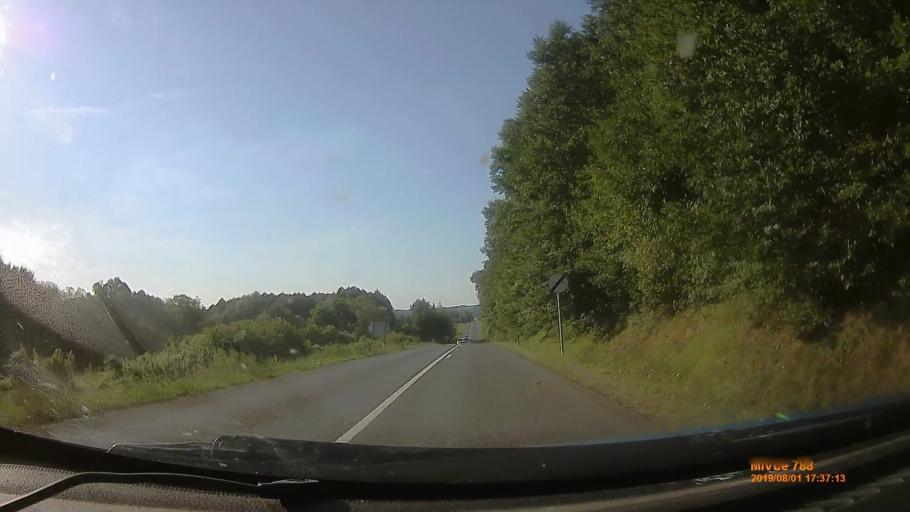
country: HU
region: Baranya
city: Komlo
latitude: 46.1839
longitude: 18.2071
